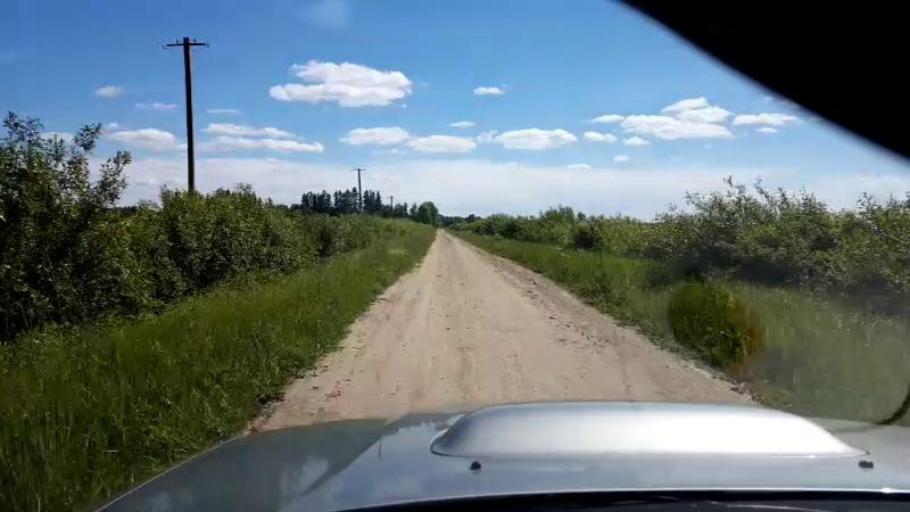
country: EE
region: Paernumaa
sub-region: Halinga vald
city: Parnu-Jaagupi
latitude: 58.5448
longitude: 24.5290
